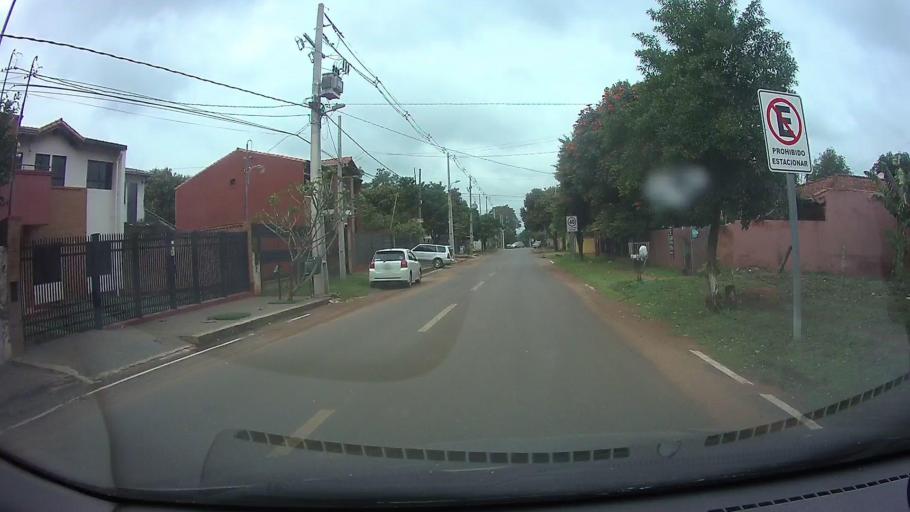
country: PY
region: Central
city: San Lorenzo
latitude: -25.3207
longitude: -57.5072
